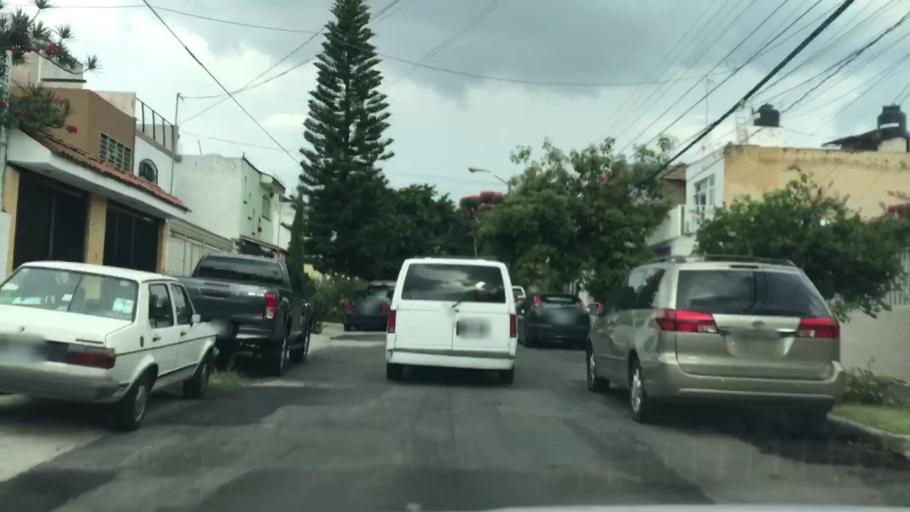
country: MX
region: Jalisco
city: Guadalajara
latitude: 20.6245
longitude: -103.4112
